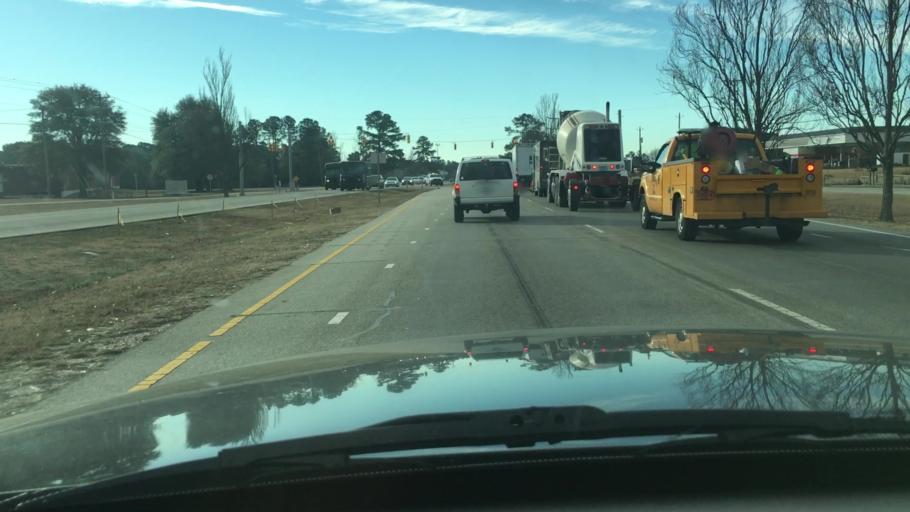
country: US
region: North Carolina
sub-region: Cumberland County
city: Fayetteville
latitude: 35.0051
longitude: -78.8992
